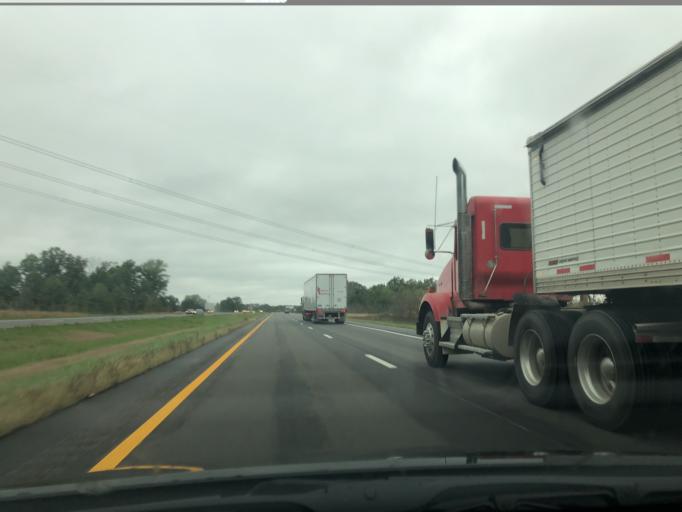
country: US
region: Ohio
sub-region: Union County
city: Marysville
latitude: 40.2428
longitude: -83.4169
